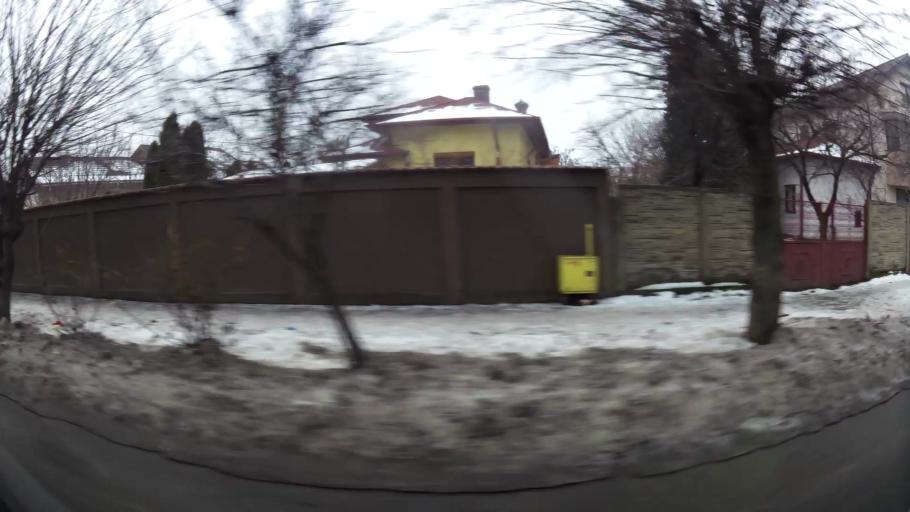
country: RO
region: Ilfov
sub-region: Comuna Chiajna
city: Rosu
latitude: 44.4508
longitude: 26.0071
